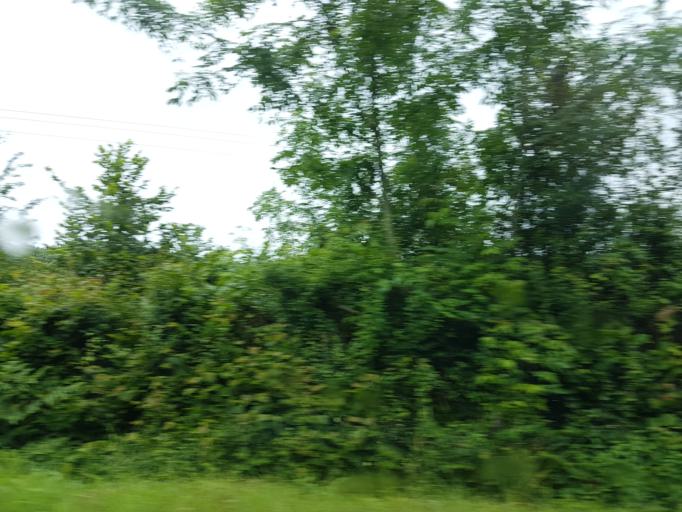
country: FR
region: Bourgogne
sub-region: Departement de la Nievre
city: Chateau-Chinon(Ville)
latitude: 47.1562
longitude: 3.8641
